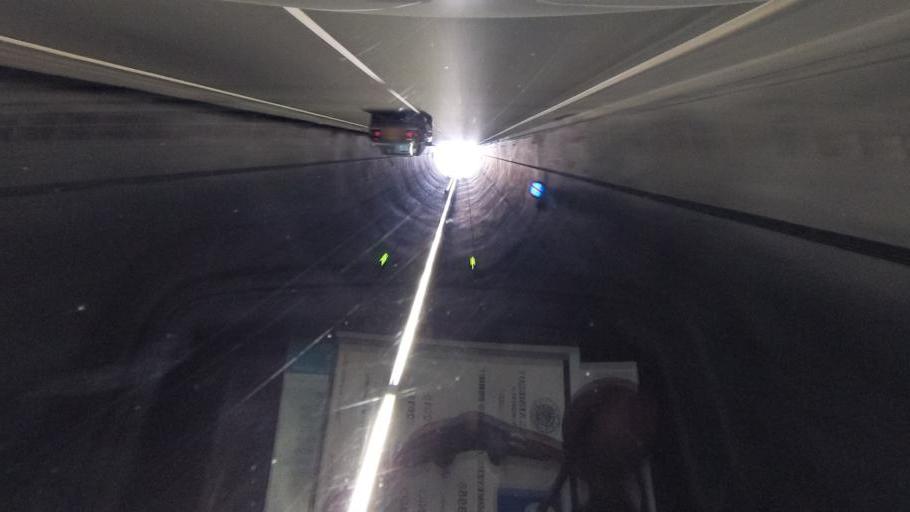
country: CY
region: Limassol
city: Sotira
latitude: 34.6994
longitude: 32.8400
